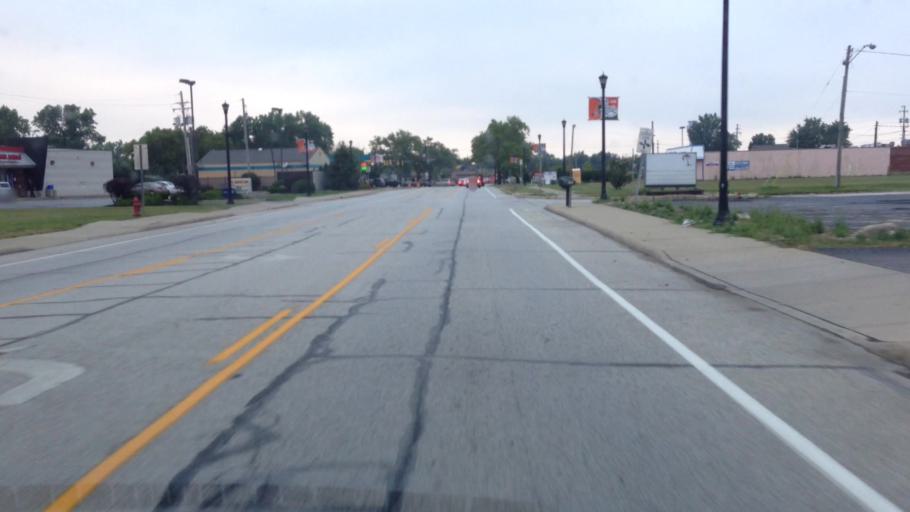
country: US
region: Ohio
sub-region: Cuyahoga County
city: Berea
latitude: 41.3865
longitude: -81.8530
